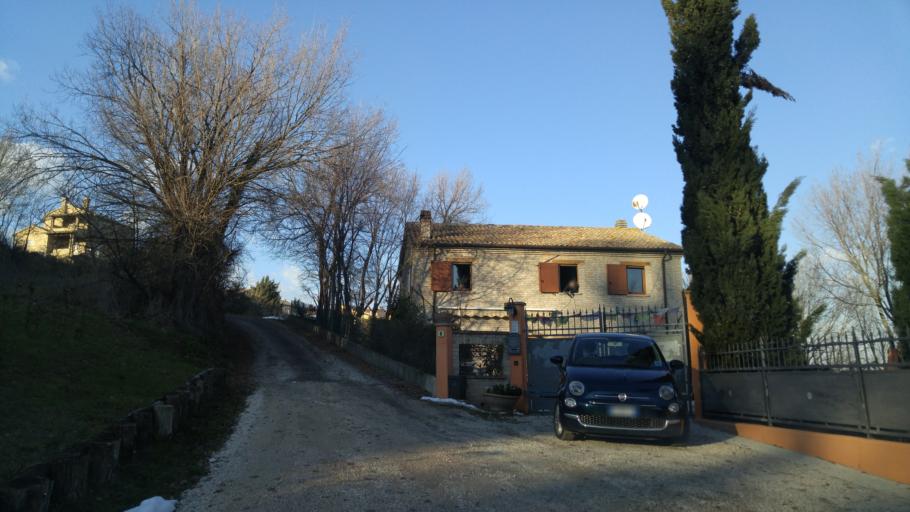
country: IT
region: The Marches
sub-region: Provincia di Pesaro e Urbino
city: Piagge
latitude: 43.7323
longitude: 12.9700
